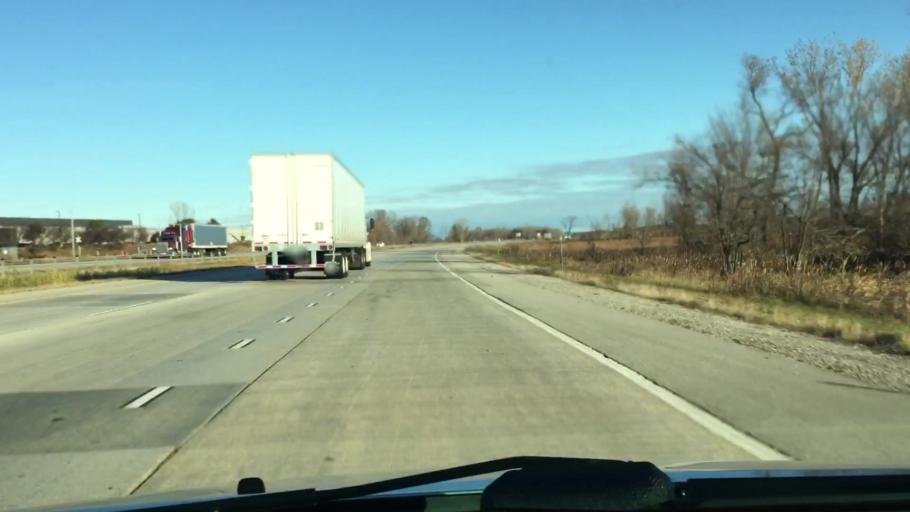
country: US
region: Wisconsin
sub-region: Dodge County
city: Lomira
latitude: 43.6222
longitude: -88.4401
